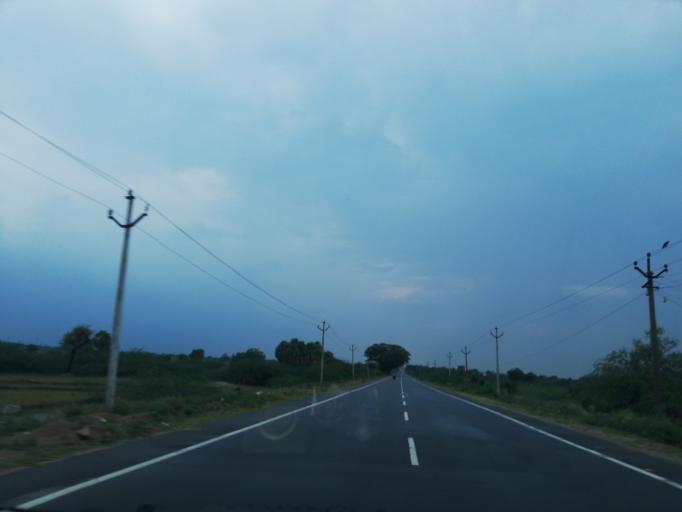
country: IN
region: Andhra Pradesh
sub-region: Guntur
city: Macherla
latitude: 16.6774
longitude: 79.2647
